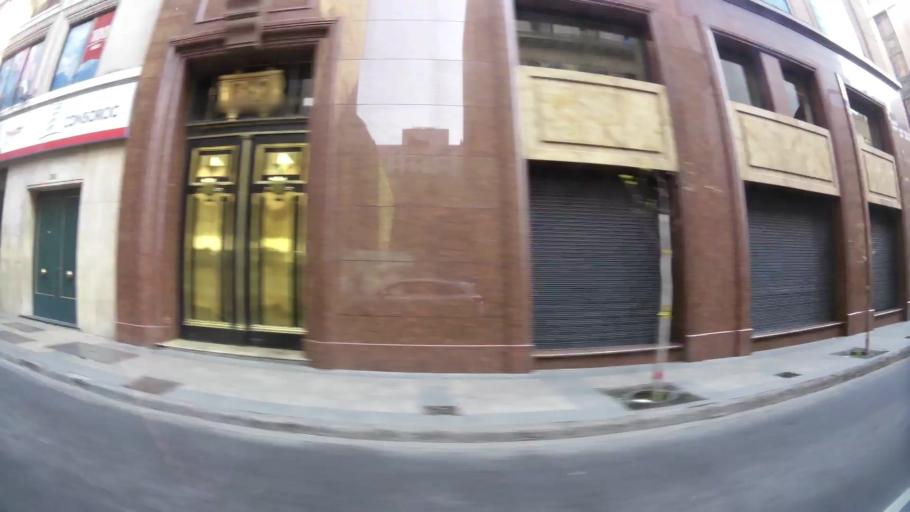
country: CL
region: Santiago Metropolitan
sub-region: Provincia de Santiago
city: Santiago
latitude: -33.4415
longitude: -70.6560
